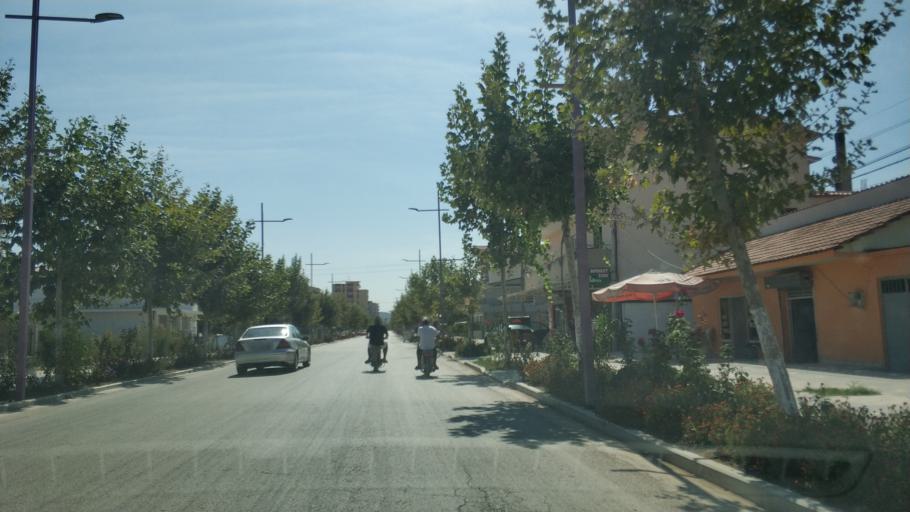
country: AL
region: Fier
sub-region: Rrethi i Lushnjes
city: Divjake
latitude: 41.0021
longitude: 19.5303
